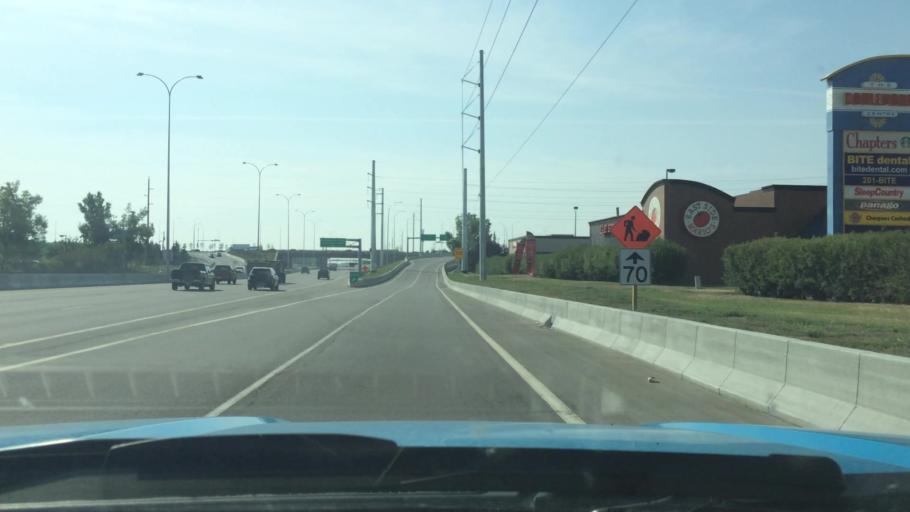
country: CA
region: Alberta
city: Calgary
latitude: 50.9084
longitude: -114.0646
